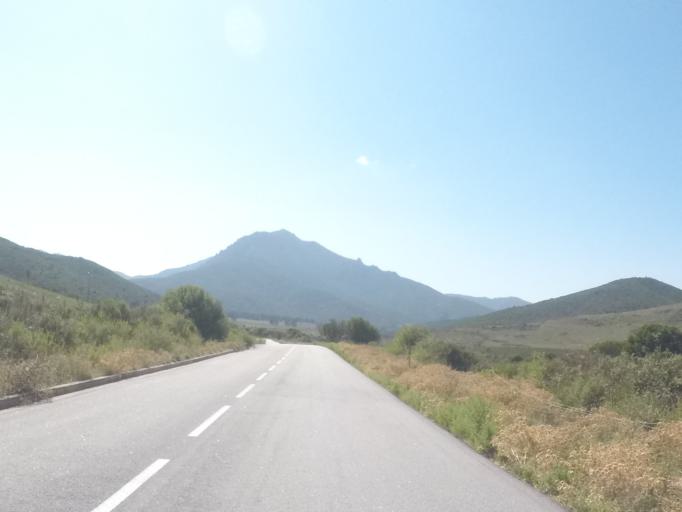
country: FR
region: Corsica
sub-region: Departement de la Haute-Corse
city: Calvi
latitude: 42.4229
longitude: 8.7210
